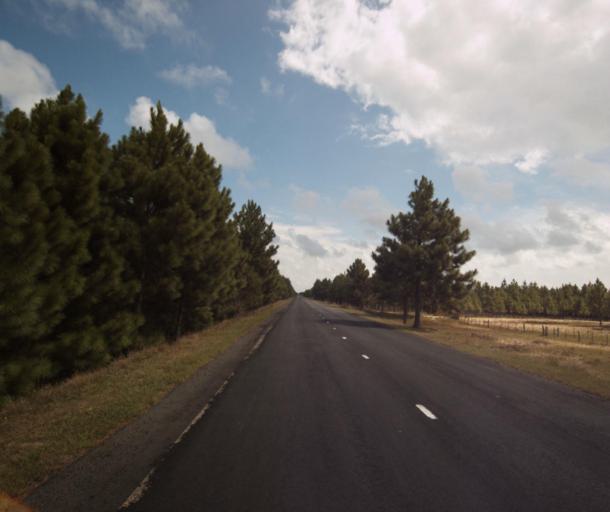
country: BR
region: Rio Grande do Sul
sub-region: Tapes
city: Tapes
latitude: -31.4139
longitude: -51.1719
